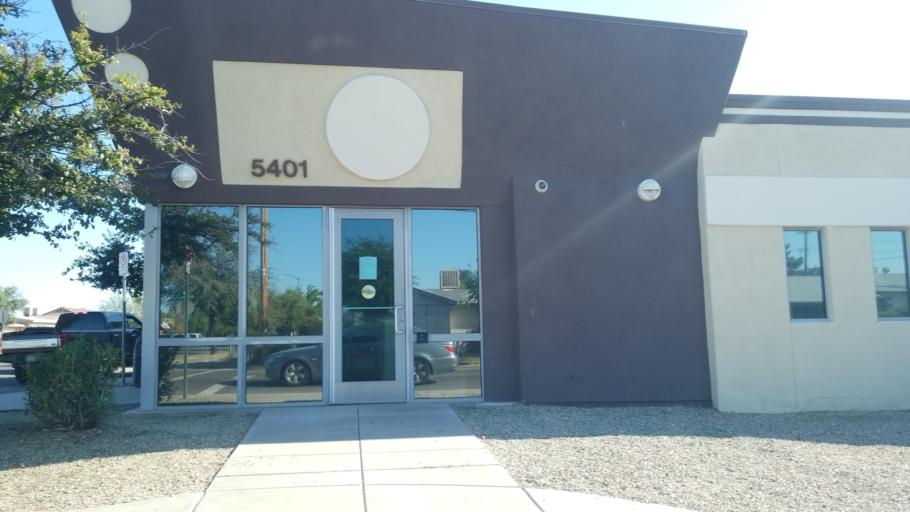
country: US
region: Arizona
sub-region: Maricopa County
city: Glendale
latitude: 33.5349
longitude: -112.1751
